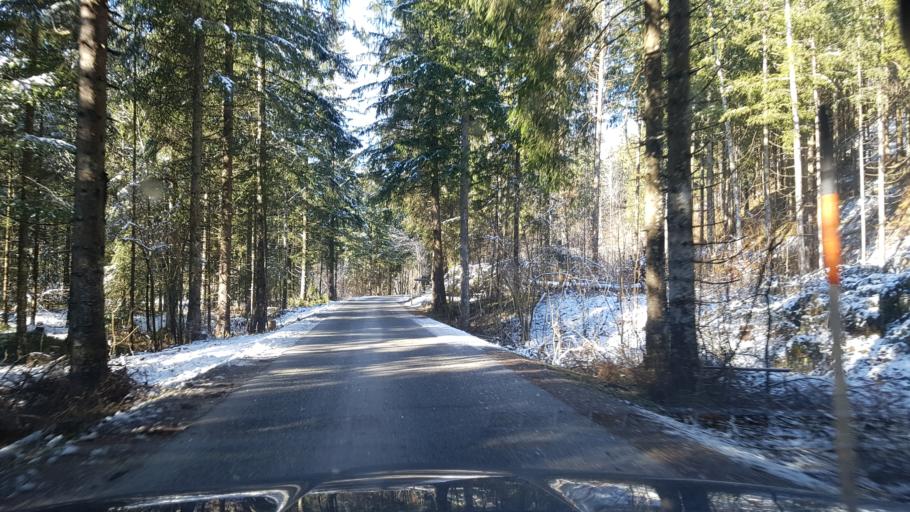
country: AT
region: Salzburg
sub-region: Politischer Bezirk Salzburg-Umgebung
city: Faistenau
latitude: 47.7688
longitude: 13.2245
